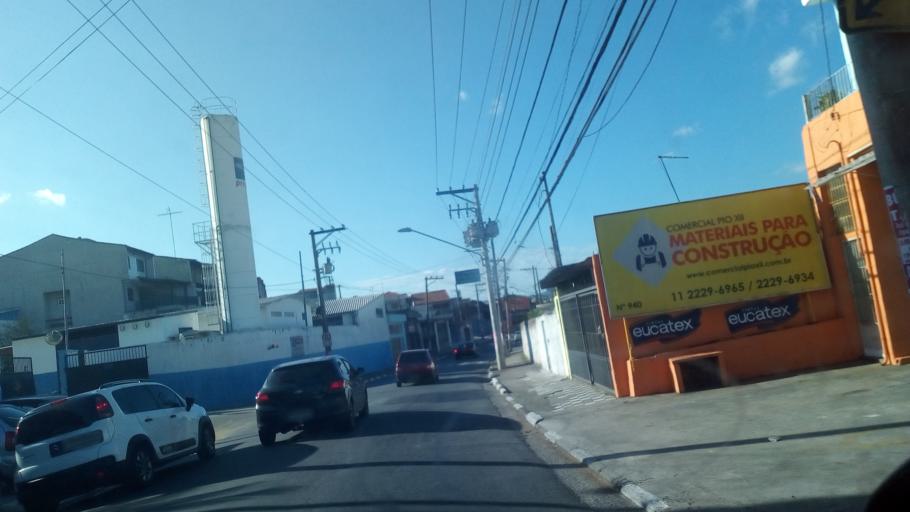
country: BR
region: Sao Paulo
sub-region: Guarulhos
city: Guarulhos
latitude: -23.4612
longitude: -46.5204
